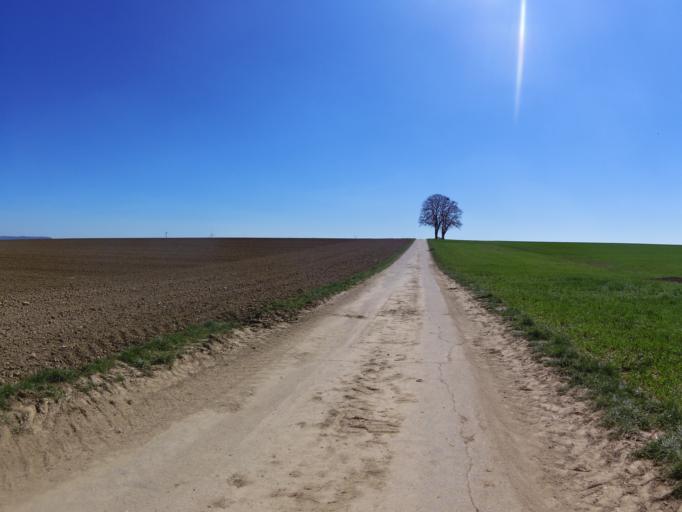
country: DE
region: Bavaria
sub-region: Regierungsbezirk Unterfranken
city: Biebelried
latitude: 49.8133
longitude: 10.0868
